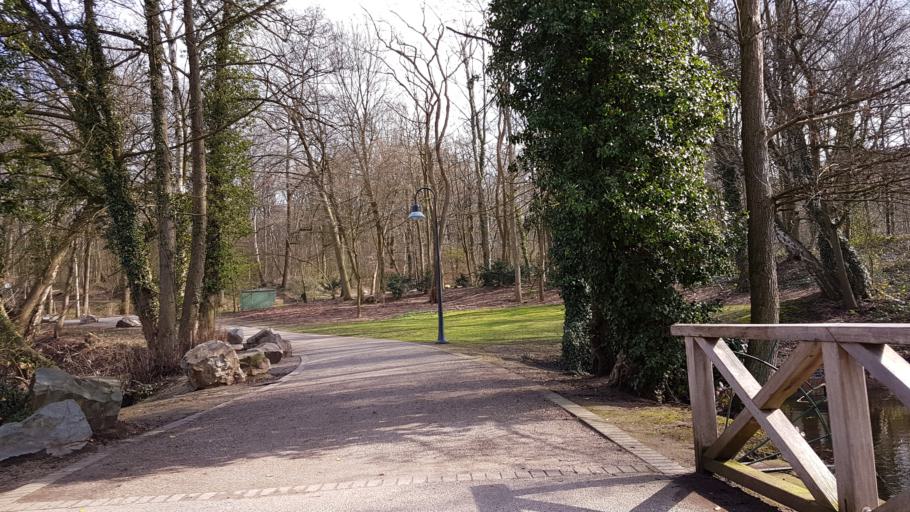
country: DE
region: North Rhine-Westphalia
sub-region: Regierungsbezirk Dusseldorf
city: Niederkruchten
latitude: 51.2187
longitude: 6.2276
